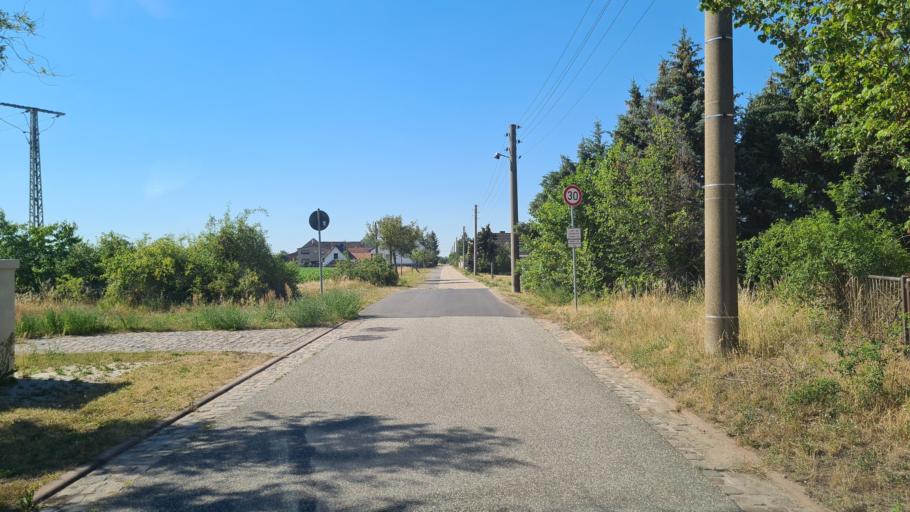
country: DE
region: Saxony-Anhalt
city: Annaburg
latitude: 51.6998
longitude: 12.9918
